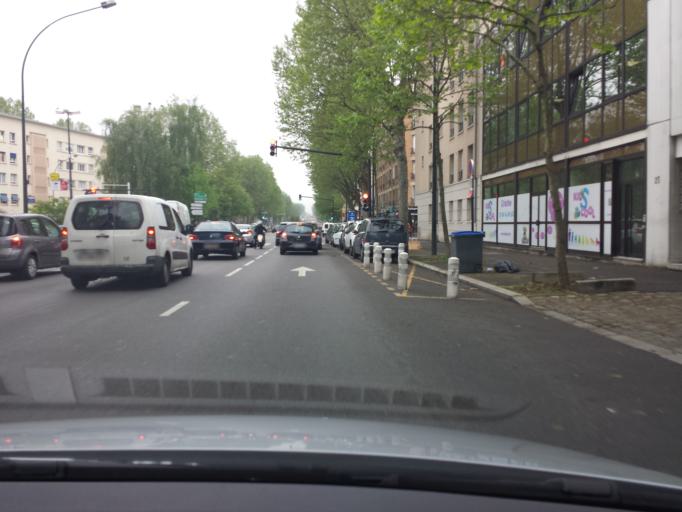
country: FR
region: Ile-de-France
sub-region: Departement des Hauts-de-Seine
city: Bourg-la-Reine
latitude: 48.7857
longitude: 2.3179
